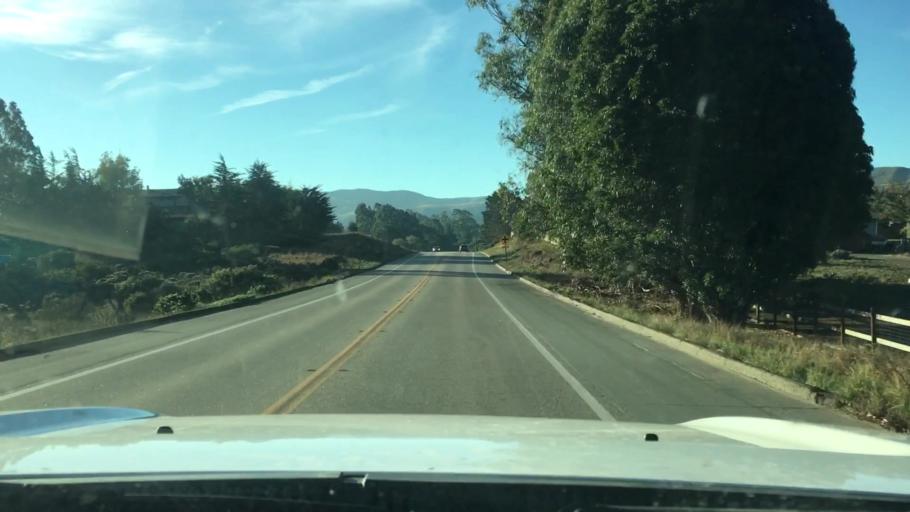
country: US
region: California
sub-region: San Luis Obispo County
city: Los Osos
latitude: 35.3187
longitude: -120.8234
